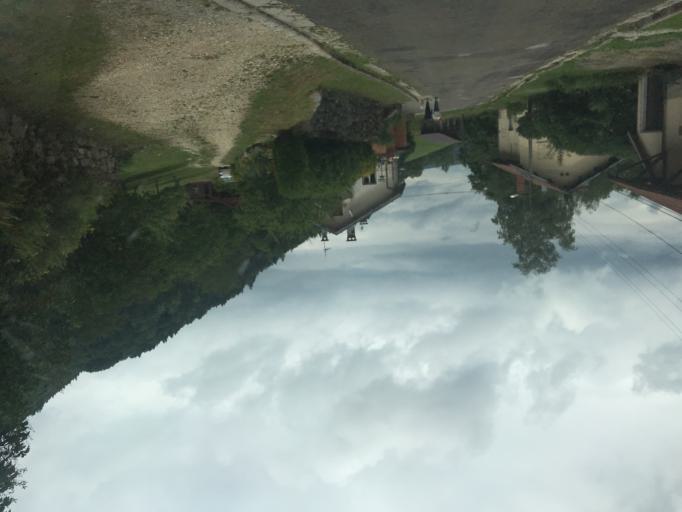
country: FR
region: Franche-Comte
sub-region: Departement du Jura
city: Saint-Claude
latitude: 46.3444
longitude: 5.8452
